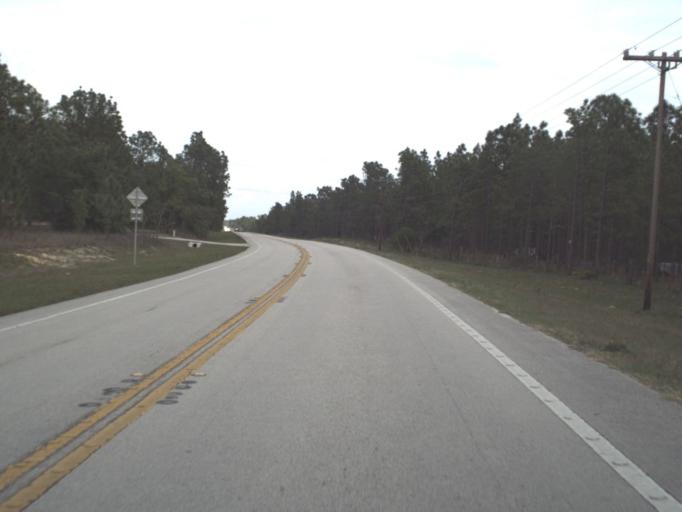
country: US
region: Florida
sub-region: Lake County
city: Mount Plymouth
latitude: 28.8528
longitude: -81.5256
